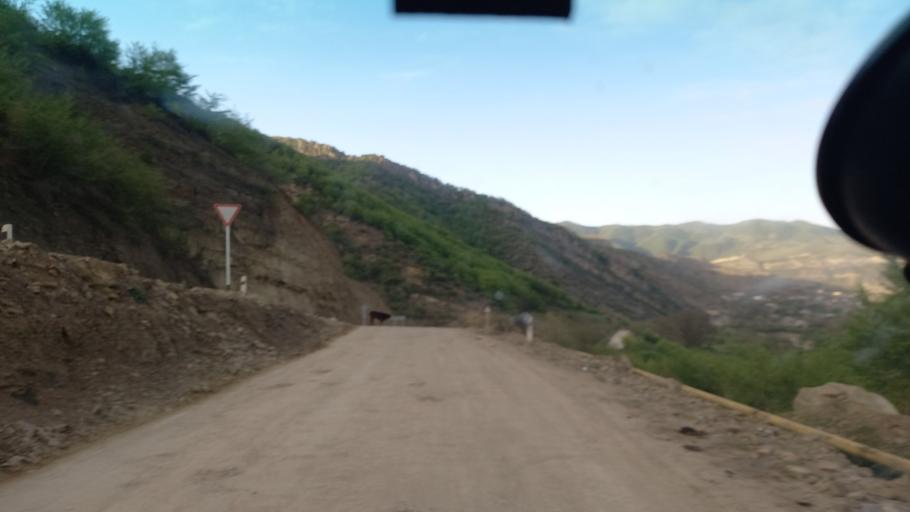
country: RU
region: Dagestan
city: Khuchni
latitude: 41.9667
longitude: 47.8741
